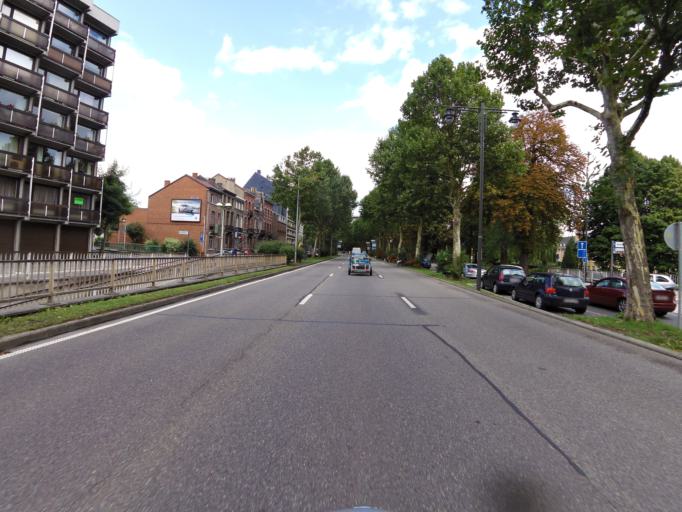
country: BE
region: Wallonia
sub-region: Province du Hainaut
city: Mons
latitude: 50.4579
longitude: 3.9605
